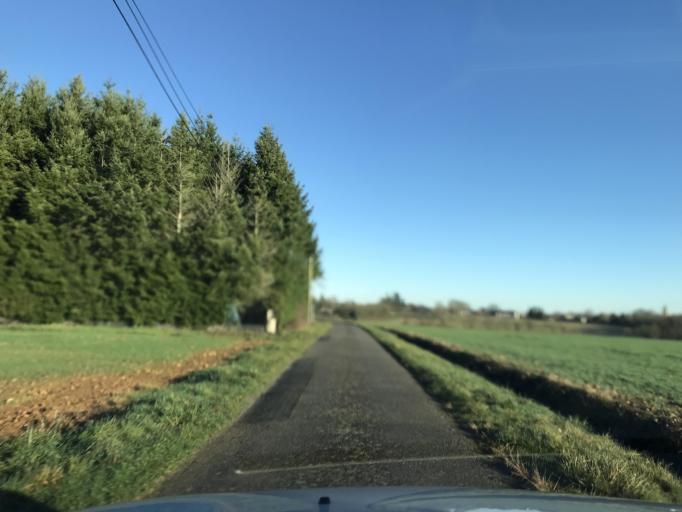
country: FR
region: Poitou-Charentes
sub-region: Departement de la Charente
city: Chasseneuil-sur-Bonnieure
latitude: 45.8452
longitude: 0.5017
